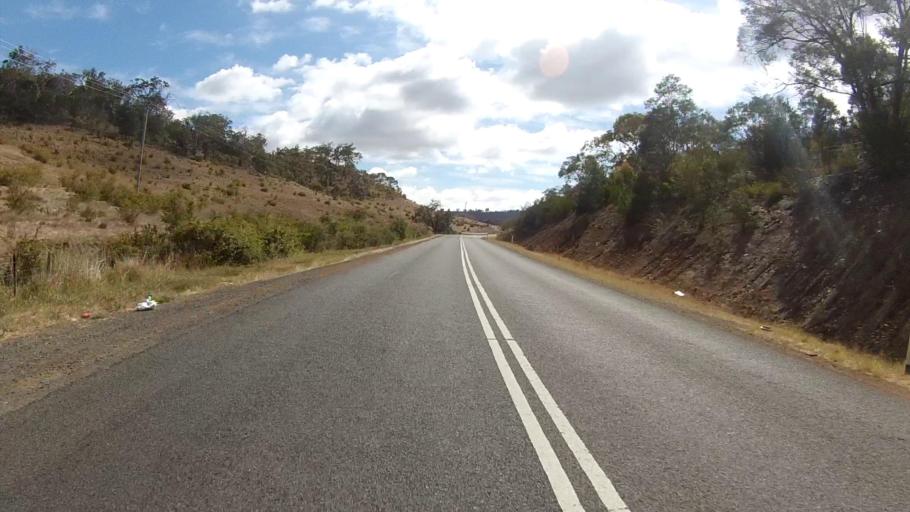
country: AU
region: Tasmania
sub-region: Brighton
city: Old Beach
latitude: -42.7438
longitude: 147.2834
